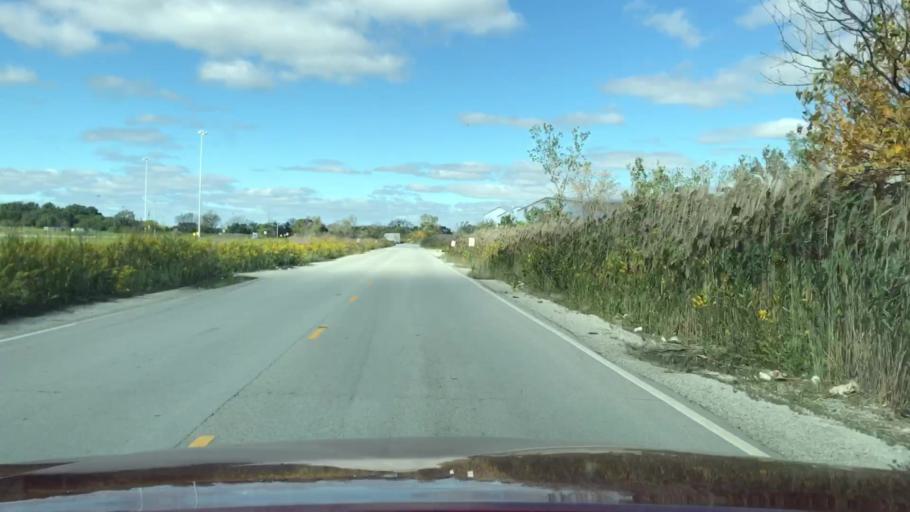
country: US
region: Illinois
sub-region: Cook County
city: Dolton
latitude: 41.6604
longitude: -87.5846
